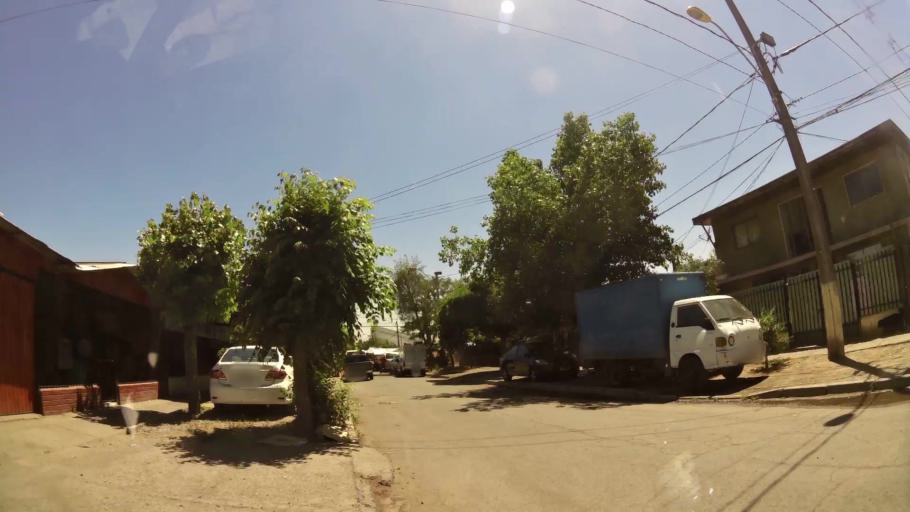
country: CL
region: Santiago Metropolitan
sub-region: Provincia de Santiago
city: La Pintana
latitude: -33.5647
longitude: -70.6646
